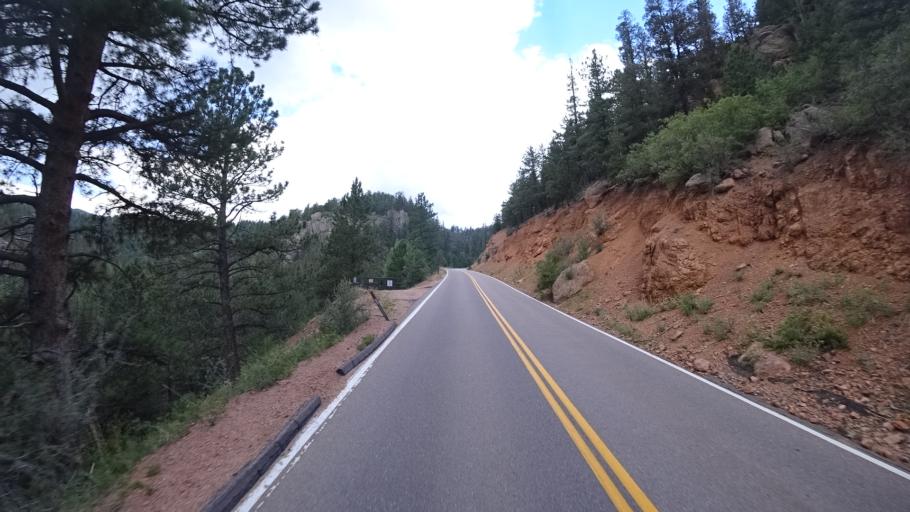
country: US
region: Colorado
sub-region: El Paso County
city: Cascade-Chipita Park
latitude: 38.8975
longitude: -104.9861
